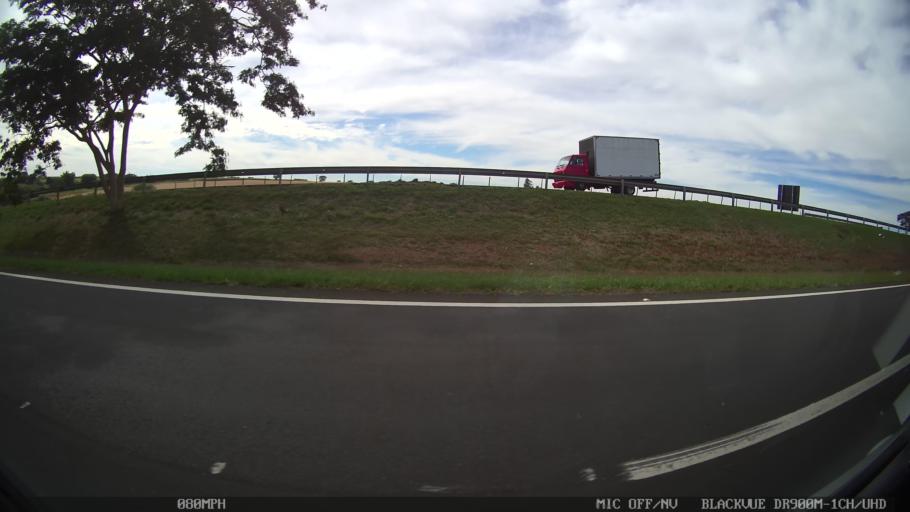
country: BR
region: Sao Paulo
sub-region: Taquaritinga
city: Taquaritinga
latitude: -21.5094
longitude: -48.5499
